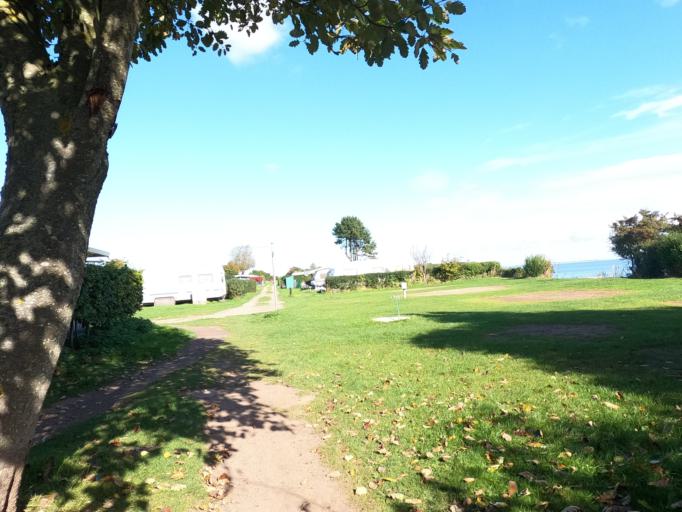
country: DE
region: Schleswig-Holstein
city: Neukirchen
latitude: 54.3196
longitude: 11.0731
